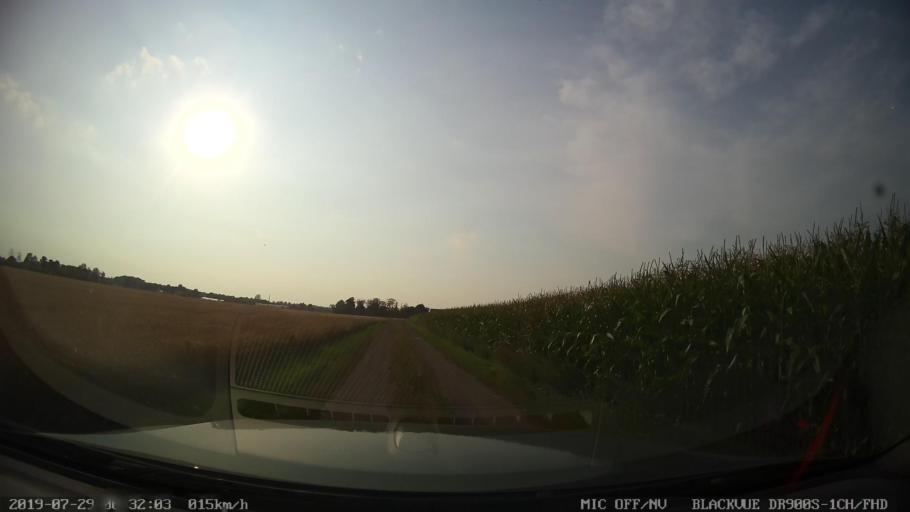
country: SE
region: Skane
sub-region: Helsingborg
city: Odakra
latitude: 56.1235
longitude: 12.7400
